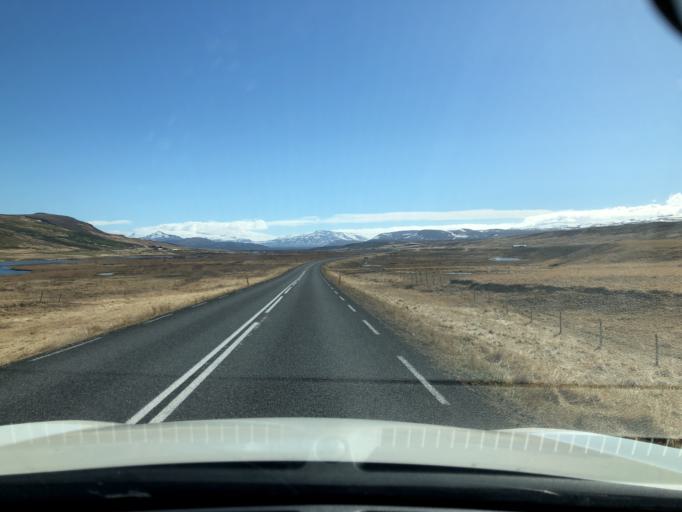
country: IS
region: South
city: Hveragerdi
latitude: 64.7026
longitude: -21.1183
